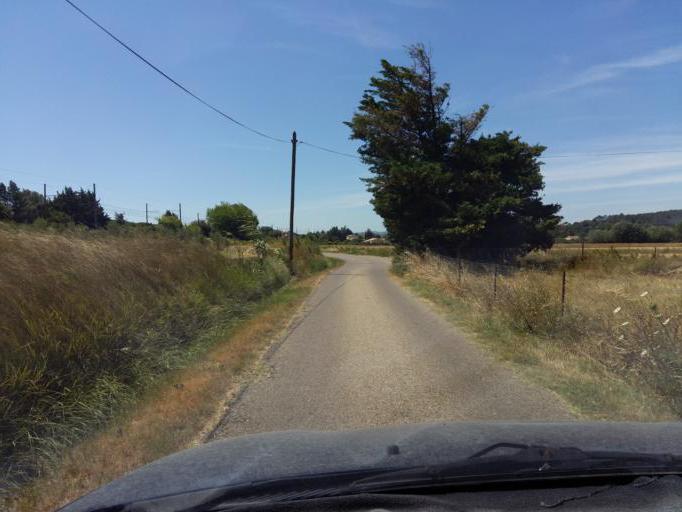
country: FR
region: Provence-Alpes-Cote d'Azur
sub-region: Departement du Vaucluse
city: Piolenc
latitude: 44.1759
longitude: 4.7770
